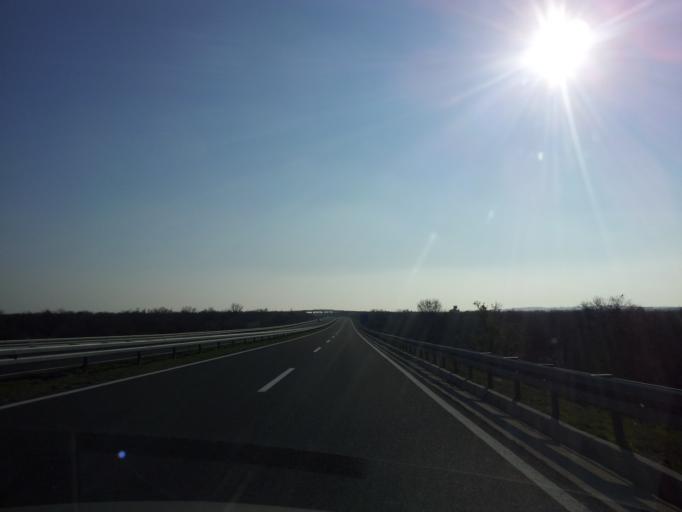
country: HR
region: Zadarska
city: Galovac
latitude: 44.0880
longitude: 15.3598
